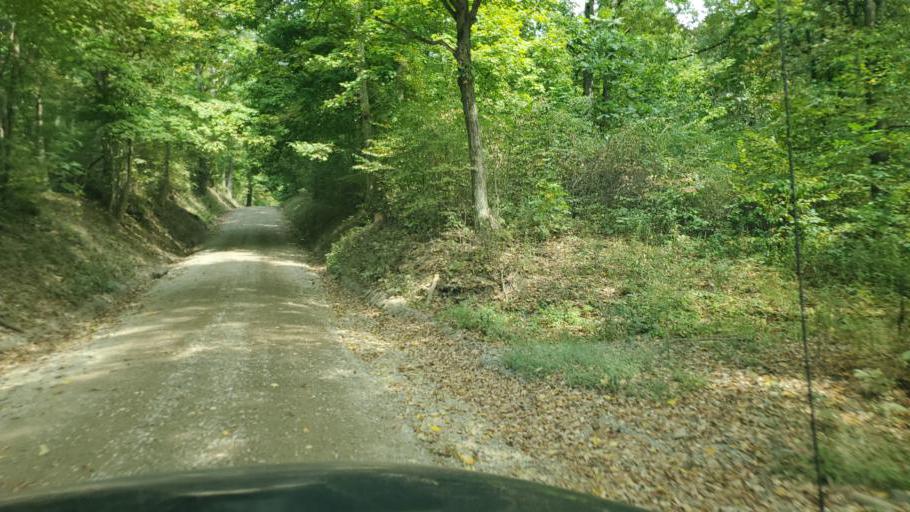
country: US
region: Ohio
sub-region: Muskingum County
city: Frazeysburg
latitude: 40.0018
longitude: -82.2025
